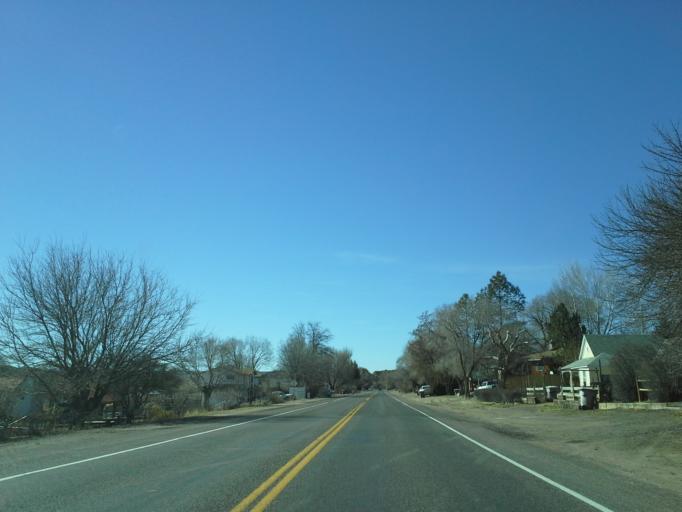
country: US
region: Utah
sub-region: Kane County
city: Kanab
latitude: 37.2494
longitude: -112.6624
